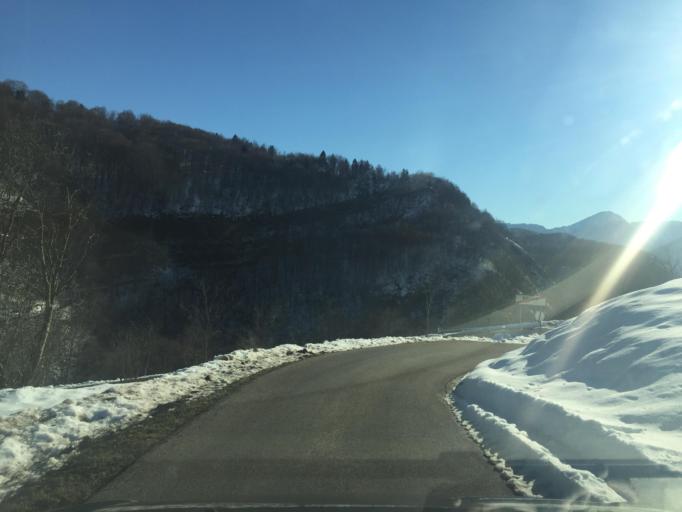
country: IT
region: Friuli Venezia Giulia
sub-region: Provincia di Udine
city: Lauco
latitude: 46.4384
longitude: 12.9685
